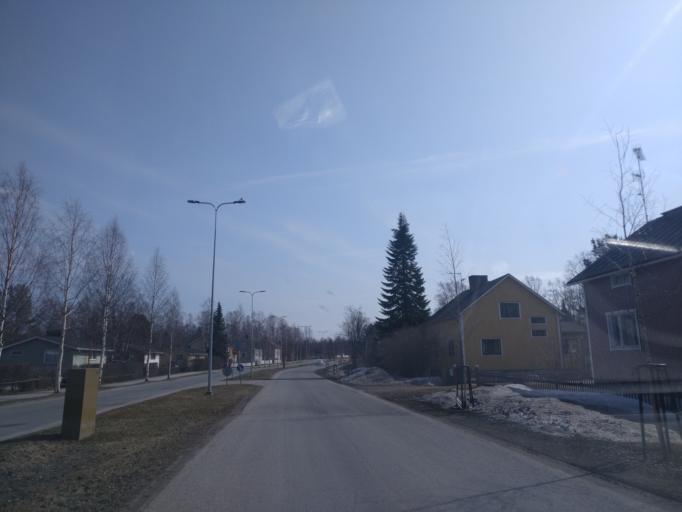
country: FI
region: Lapland
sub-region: Kemi-Tornio
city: Kemi
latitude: 65.7287
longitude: 24.6080
